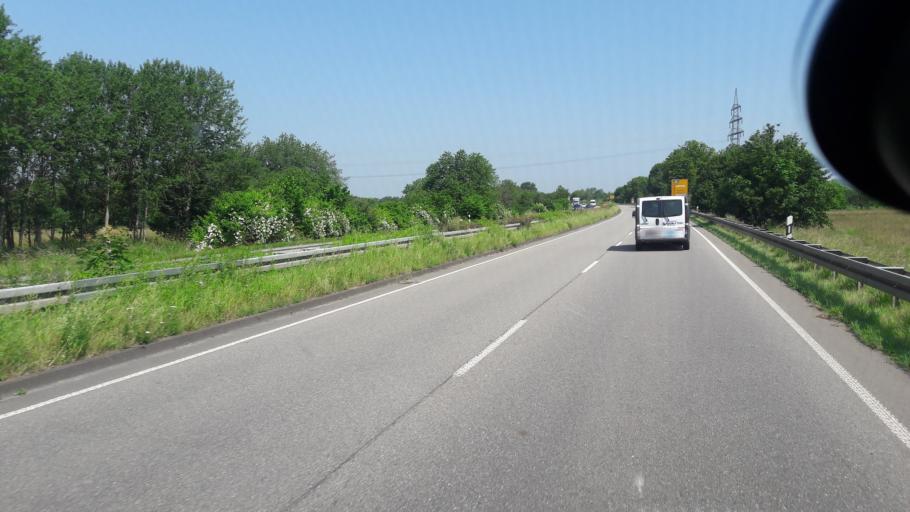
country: DE
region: Baden-Wuerttemberg
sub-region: Karlsruhe Region
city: Bischweier
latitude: 48.8474
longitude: 8.2679
